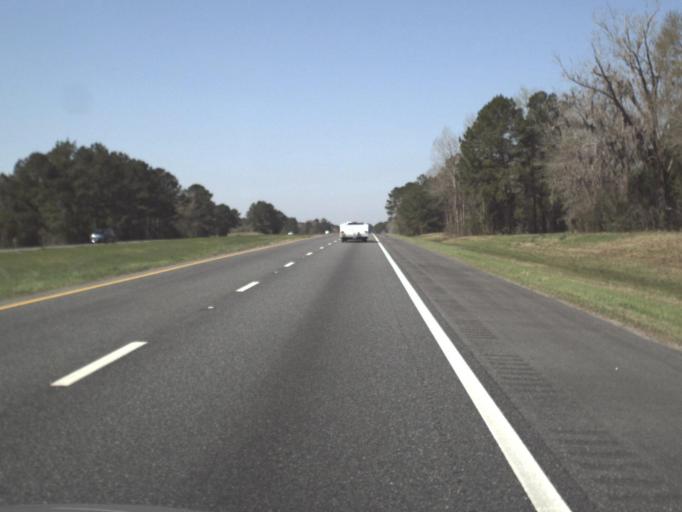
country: US
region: Florida
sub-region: Jackson County
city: Marianna
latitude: 30.7579
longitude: -85.2934
